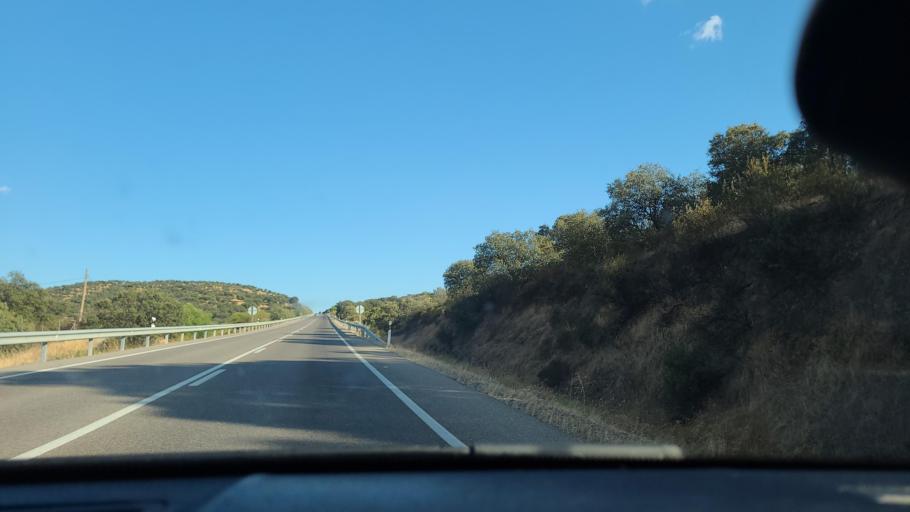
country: ES
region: Andalusia
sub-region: Province of Cordoba
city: Espiel
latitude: 38.1995
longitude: -5.1036
